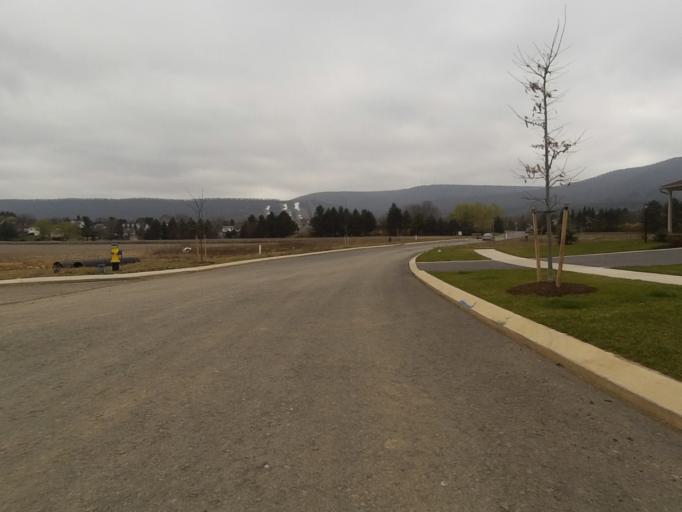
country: US
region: Pennsylvania
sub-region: Centre County
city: Boalsburg
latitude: 40.7860
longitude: -77.7697
